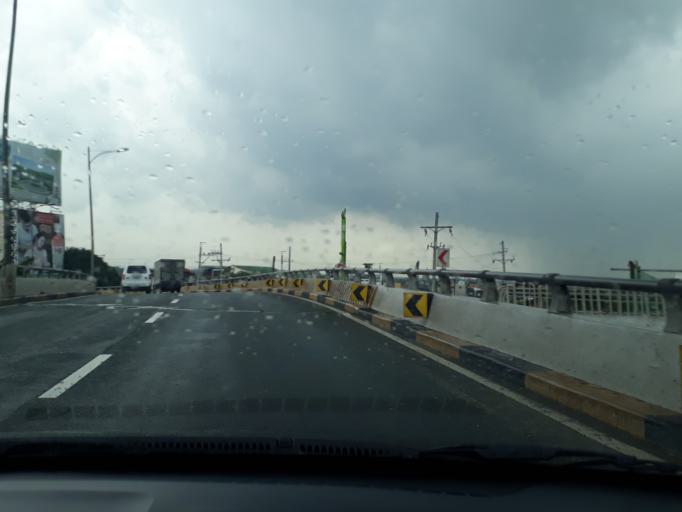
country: PH
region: Metro Manila
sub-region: Makati City
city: Makati City
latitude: 14.5118
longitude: 121.0328
